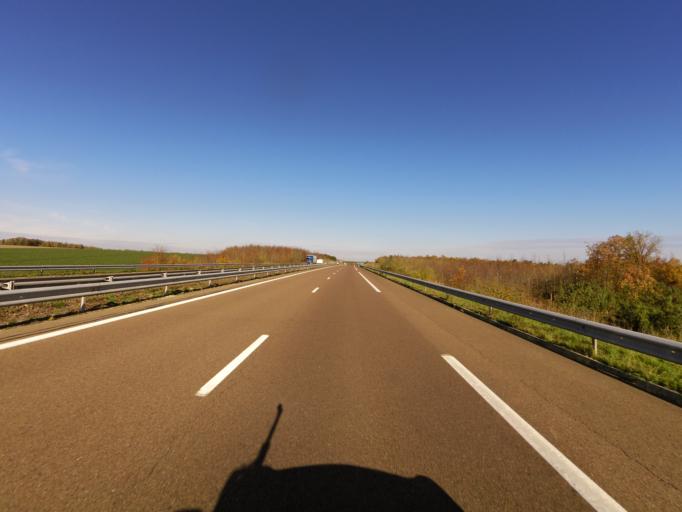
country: FR
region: Champagne-Ardenne
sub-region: Departement de la Marne
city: Fagnieres
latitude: 48.8957
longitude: 4.2869
